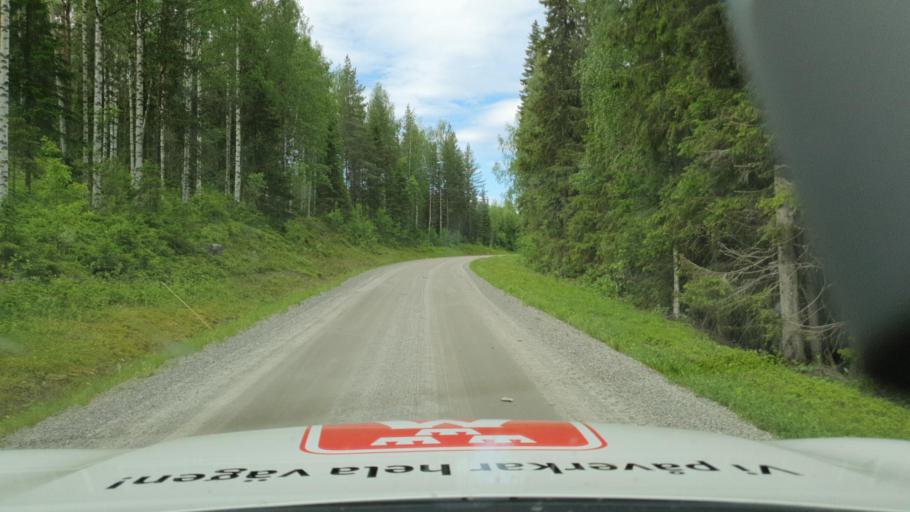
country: SE
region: Vaesterbotten
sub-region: Norsjo Kommun
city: Norsjoe
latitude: 64.8004
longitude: 19.6649
